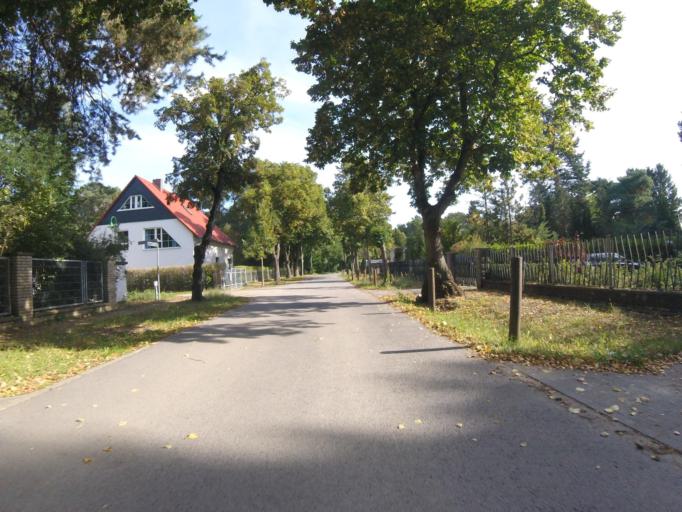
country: DE
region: Brandenburg
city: Bestensee
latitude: 52.2978
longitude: 13.7103
